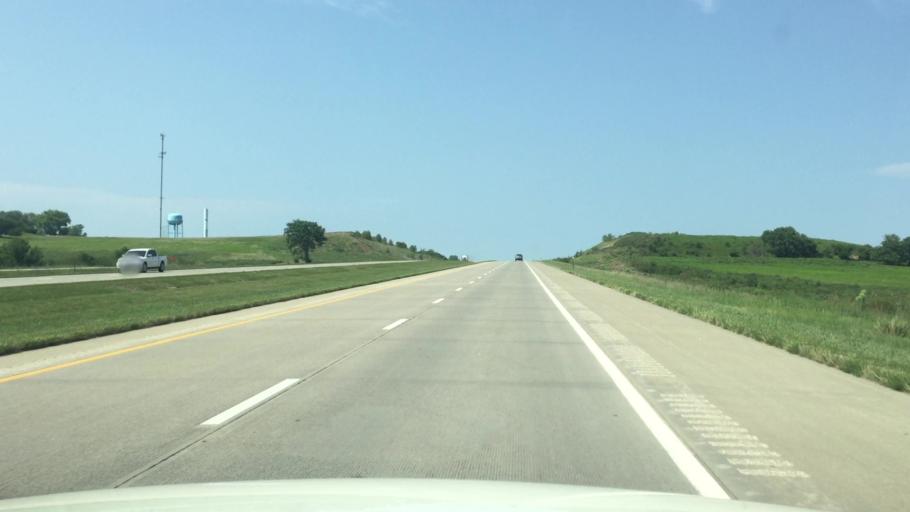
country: US
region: Kansas
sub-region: Linn County
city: Pleasanton
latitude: 38.1024
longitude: -94.7133
